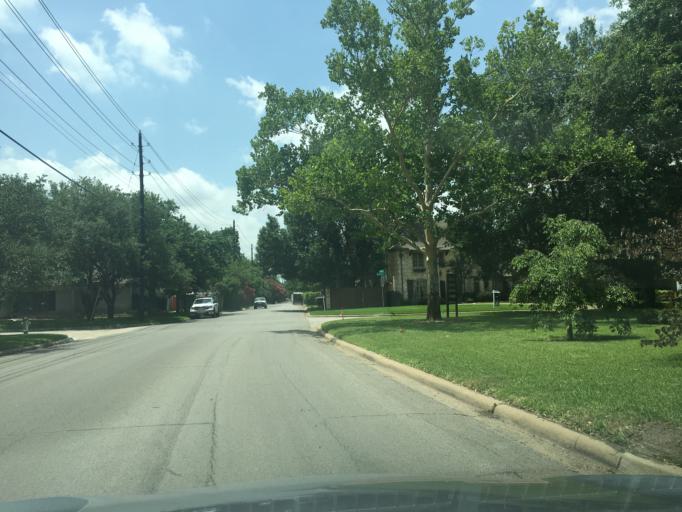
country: US
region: Texas
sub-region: Dallas County
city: University Park
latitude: 32.8785
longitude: -96.7903
